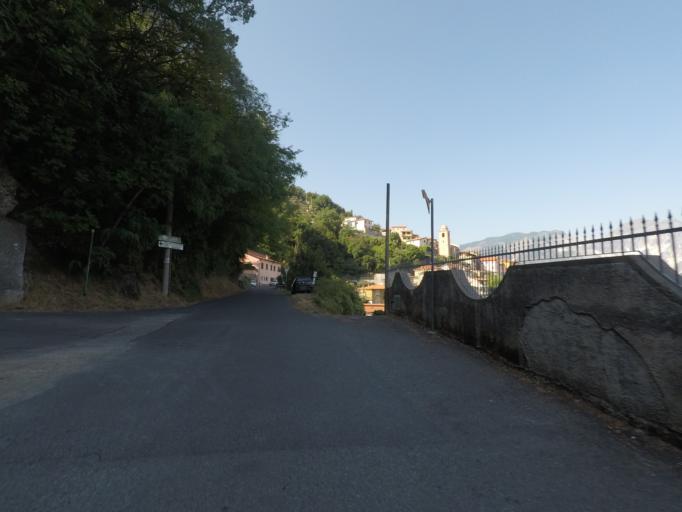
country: IT
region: Tuscany
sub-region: Provincia di Massa-Carrara
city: Carrara
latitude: 44.0742
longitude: 10.0644
